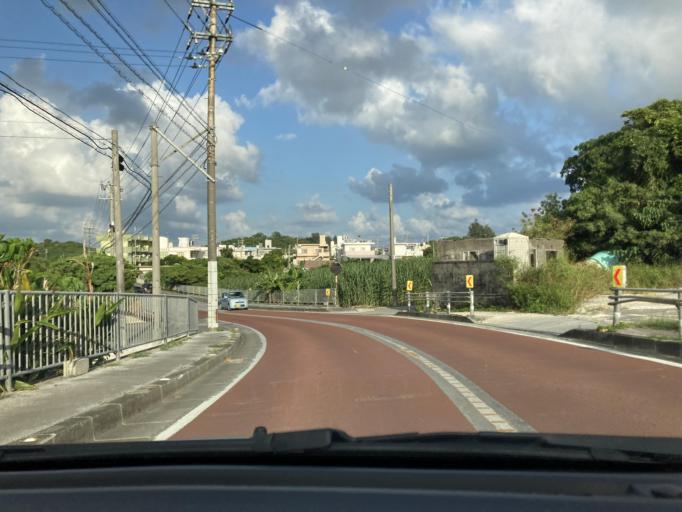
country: JP
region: Okinawa
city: Itoman
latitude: 26.1366
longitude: 127.6955
